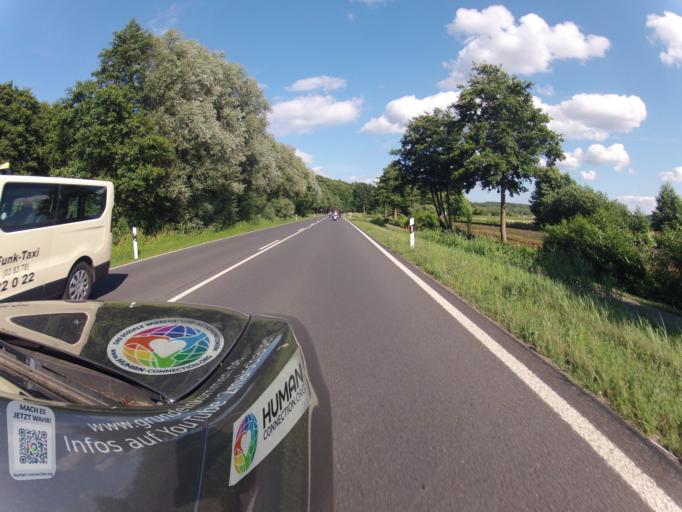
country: DE
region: Mecklenburg-Vorpommern
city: Seebad Bansin
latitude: 53.9801
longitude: 14.0933
